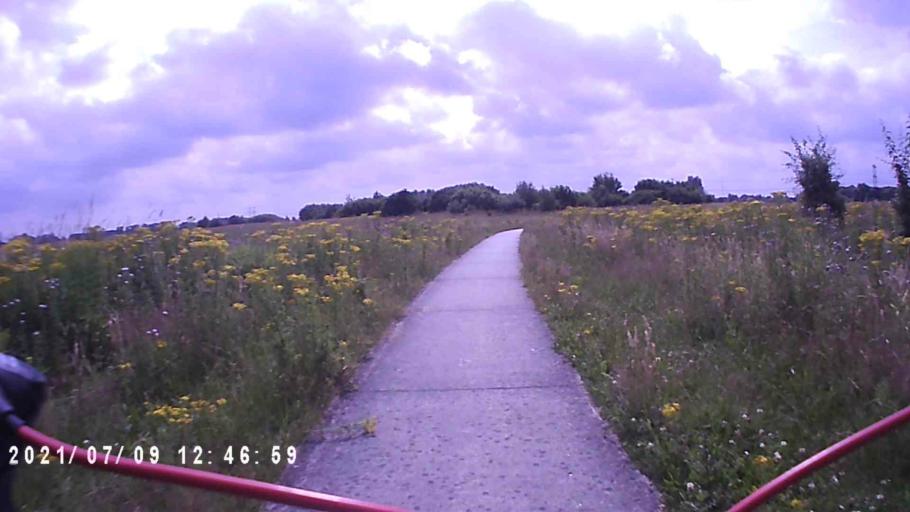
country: NL
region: Groningen
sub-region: Gemeente  Oldambt
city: Winschoten
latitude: 53.1283
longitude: 7.0314
